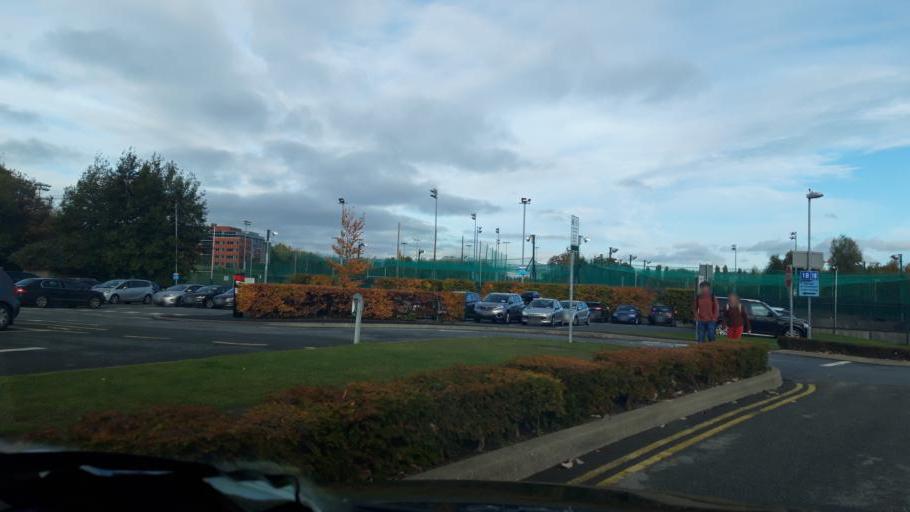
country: IE
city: Clonskeagh
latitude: 53.3085
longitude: -6.2303
